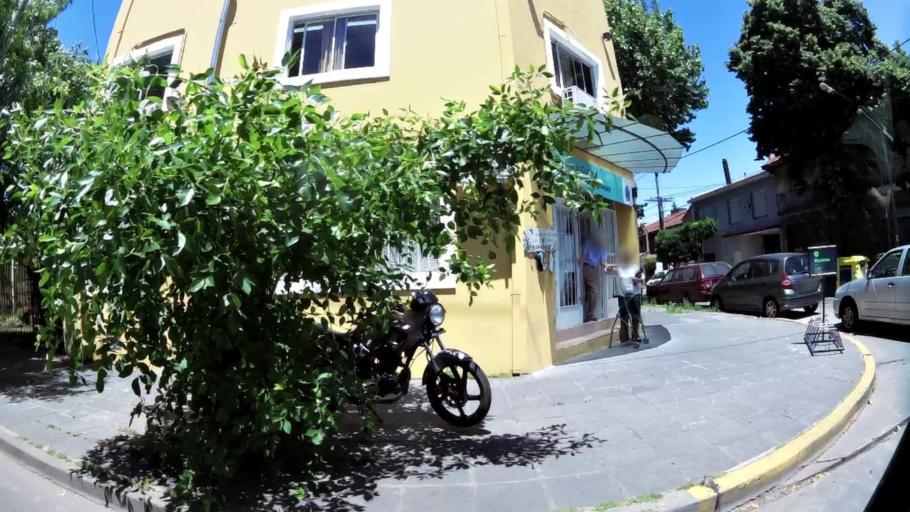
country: AR
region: Buenos Aires
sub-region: Partido de San Isidro
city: San Isidro
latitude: -34.4929
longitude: -58.5135
